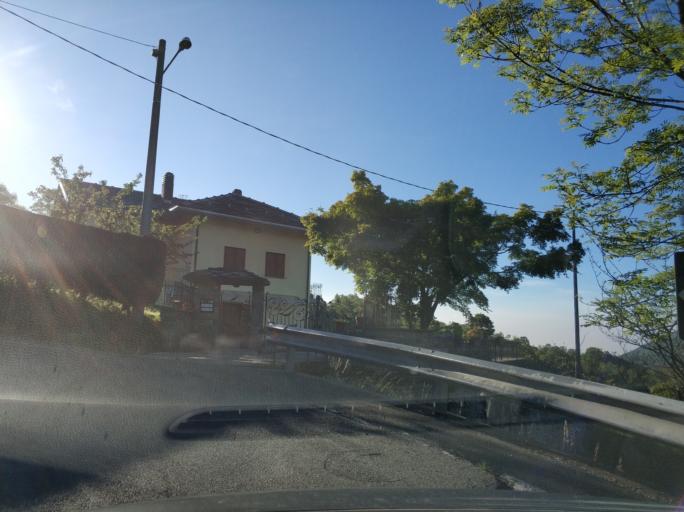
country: IT
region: Piedmont
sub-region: Provincia di Torino
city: Coassolo
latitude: 45.2926
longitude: 7.4700
